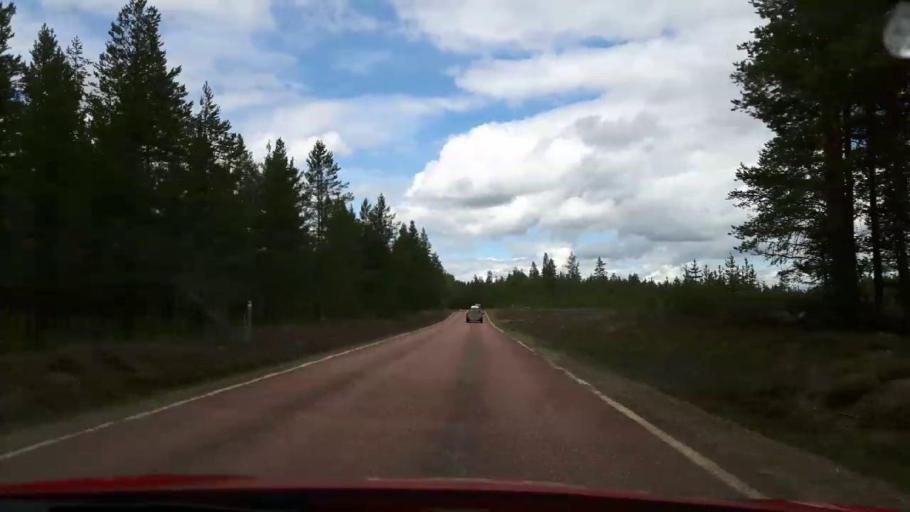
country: NO
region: Hedmark
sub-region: Trysil
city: Innbygda
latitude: 61.8471
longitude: 12.9546
